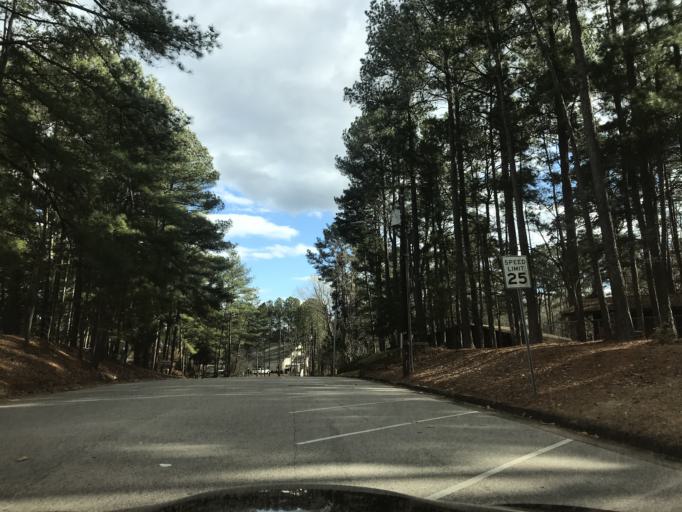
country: US
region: North Carolina
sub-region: Wake County
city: West Raleigh
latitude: 35.8549
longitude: -78.7044
